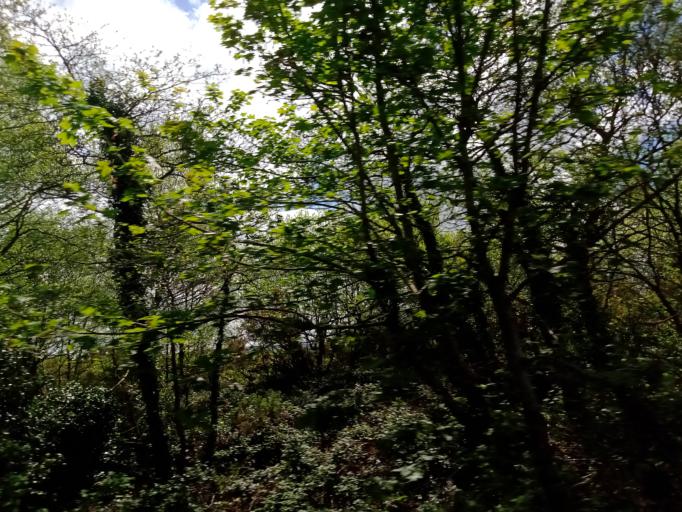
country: IE
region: Munster
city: Thurles
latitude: 52.6824
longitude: -7.6620
